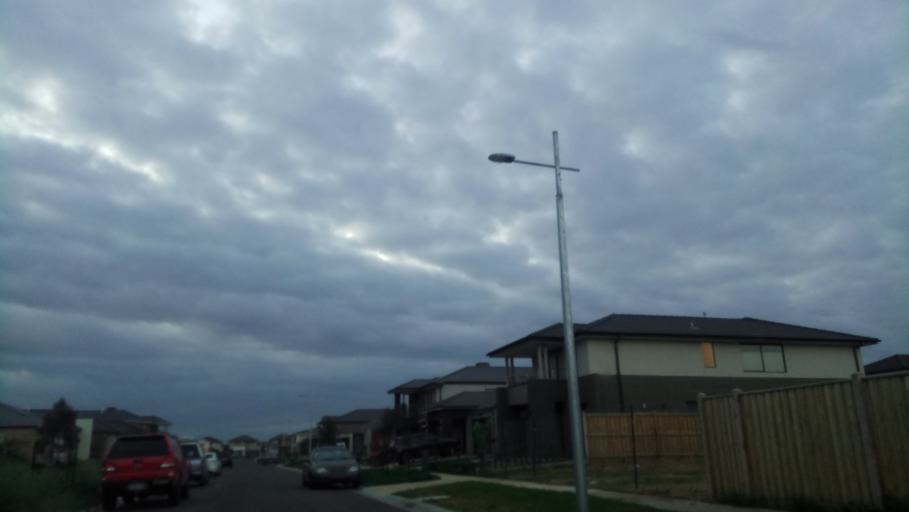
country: AU
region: Victoria
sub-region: Wyndham
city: Point Cook
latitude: -37.9143
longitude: 144.7629
